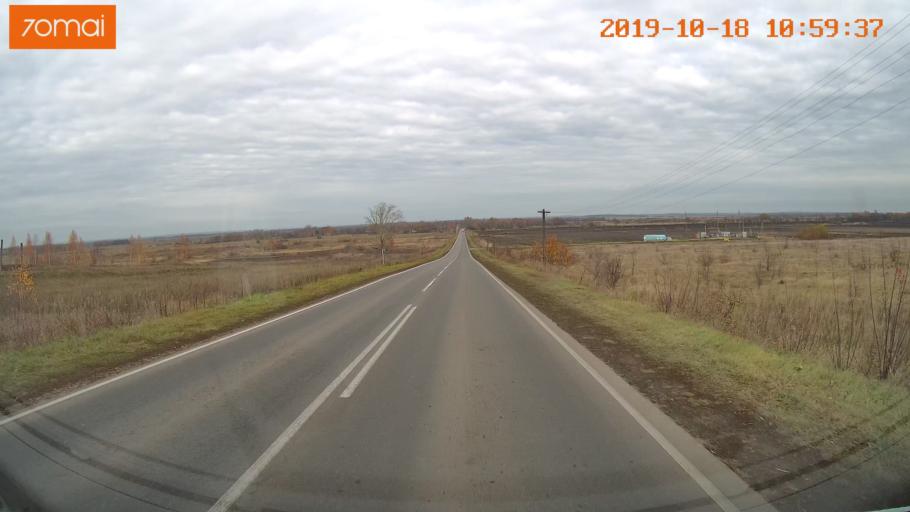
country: RU
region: Tula
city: Yepifan'
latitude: 53.8319
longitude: 38.5566
